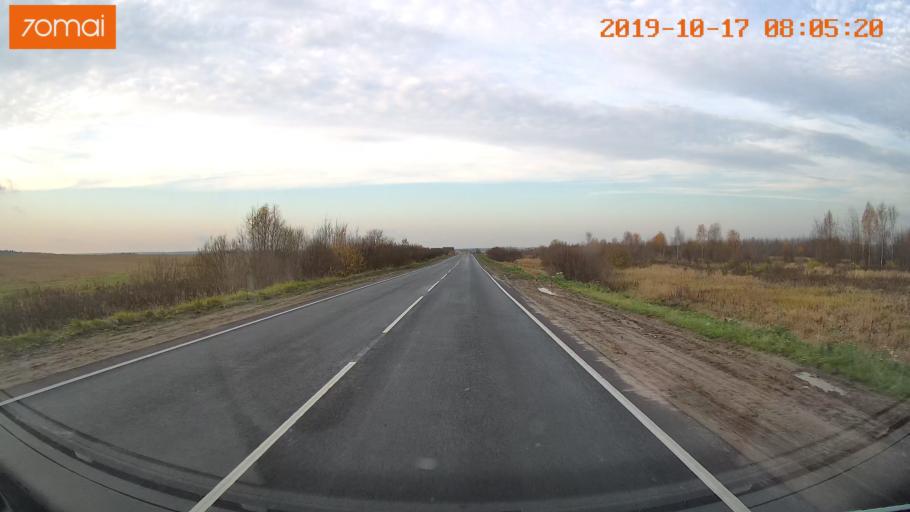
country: RU
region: Vladimir
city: Kol'chugino
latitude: 56.3357
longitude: 39.4177
